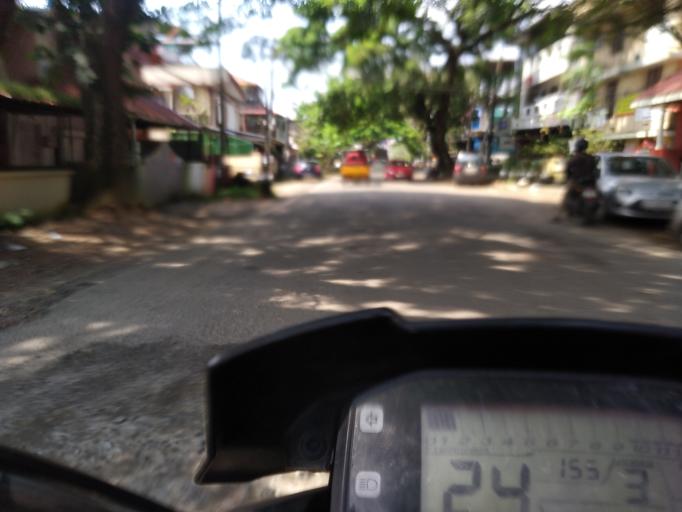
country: IN
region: Kerala
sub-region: Ernakulam
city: Cochin
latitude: 9.9763
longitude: 76.2945
